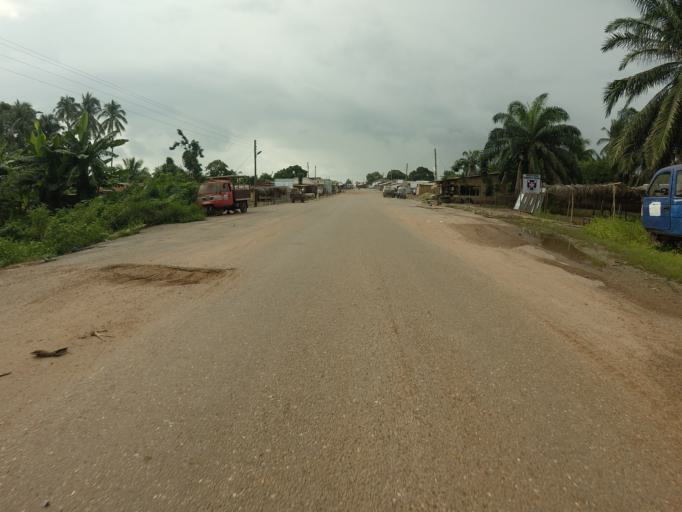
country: GH
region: Volta
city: Kpandu
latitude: 6.9957
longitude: 0.4390
